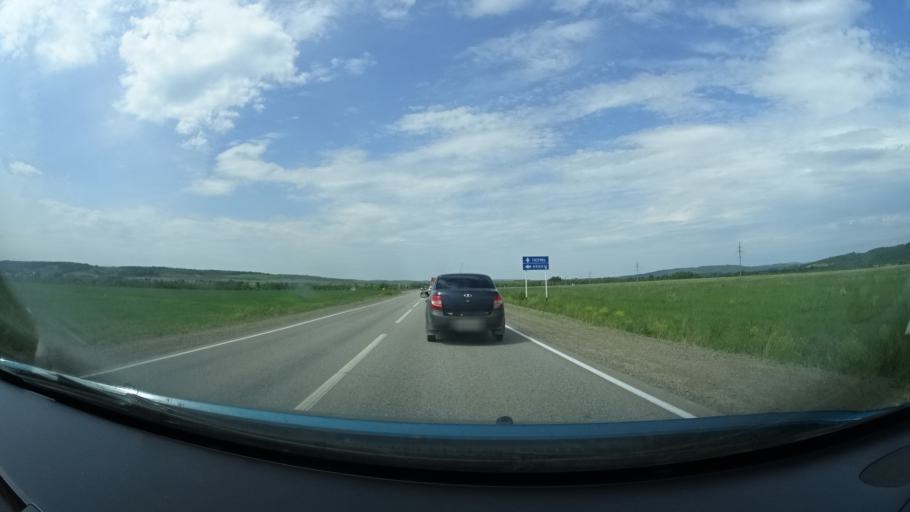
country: RU
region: Perm
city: Barda
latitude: 57.0186
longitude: 55.5573
